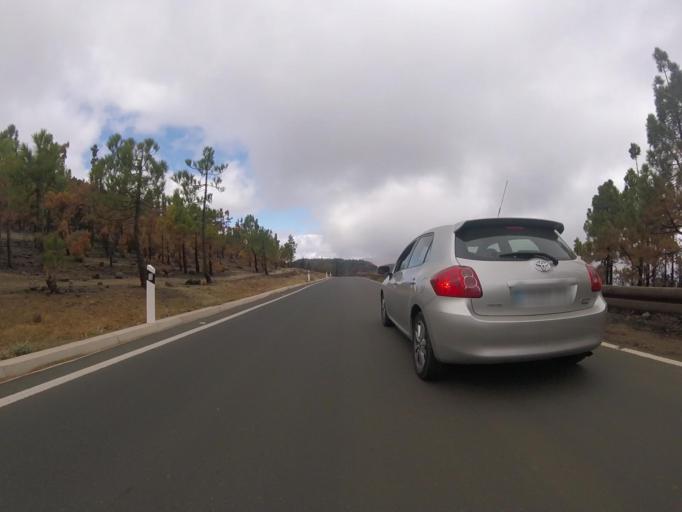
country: ES
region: Canary Islands
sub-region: Provincia de Las Palmas
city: San Bartolome
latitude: 27.9693
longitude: -15.5685
